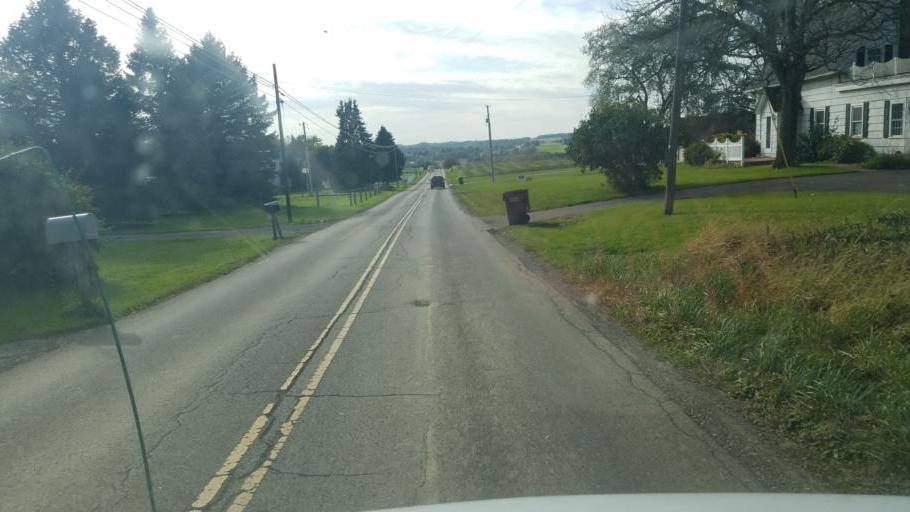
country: US
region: Ohio
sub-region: Wayne County
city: Apple Creek
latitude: 40.6880
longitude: -81.8460
